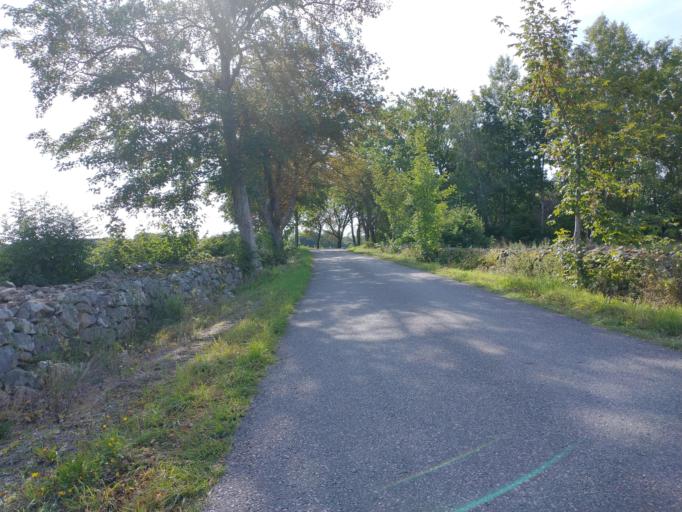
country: SE
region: Kalmar
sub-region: Kalmar Kommun
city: Lindsdal
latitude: 56.7779
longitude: 16.3234
